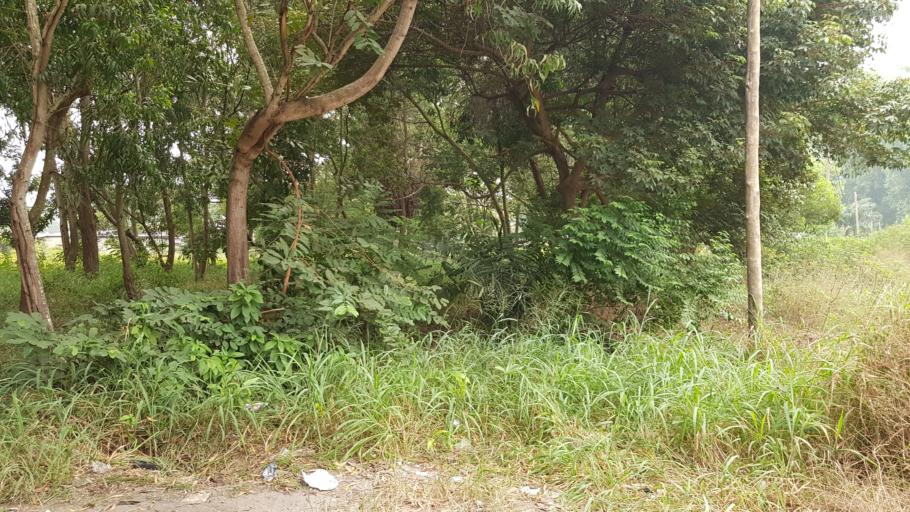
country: CG
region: Brazzaville
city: Brazzaville
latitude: -4.2666
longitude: 15.2508
